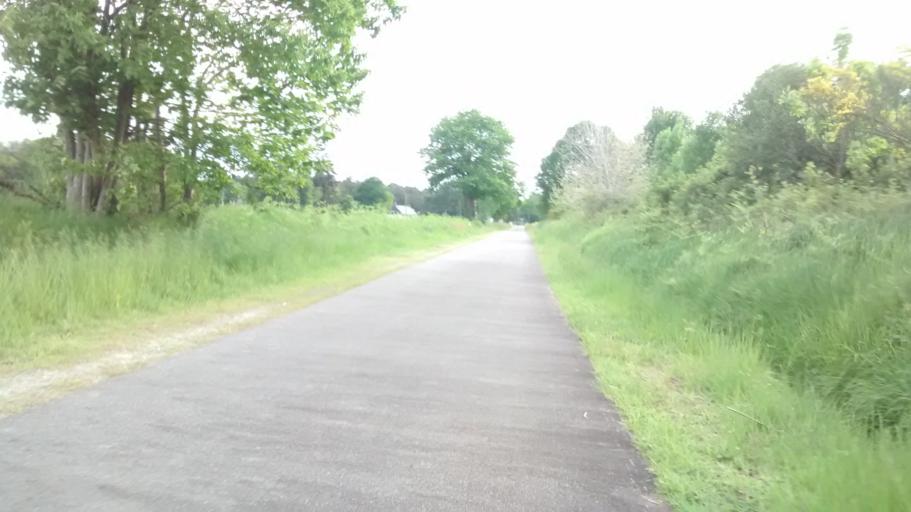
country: FR
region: Brittany
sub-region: Departement du Morbihan
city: Pleucadeuc
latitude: 47.7475
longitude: -2.4049
